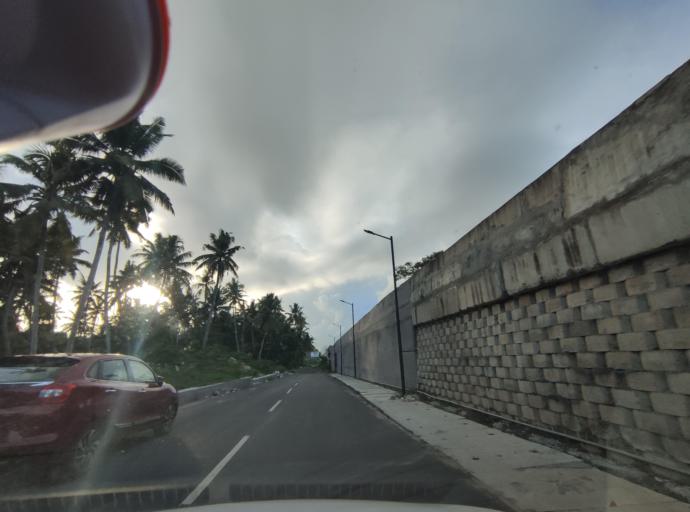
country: IN
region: Kerala
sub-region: Thiruvananthapuram
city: Thiruvananthapuram
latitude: 8.5179
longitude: 76.8975
